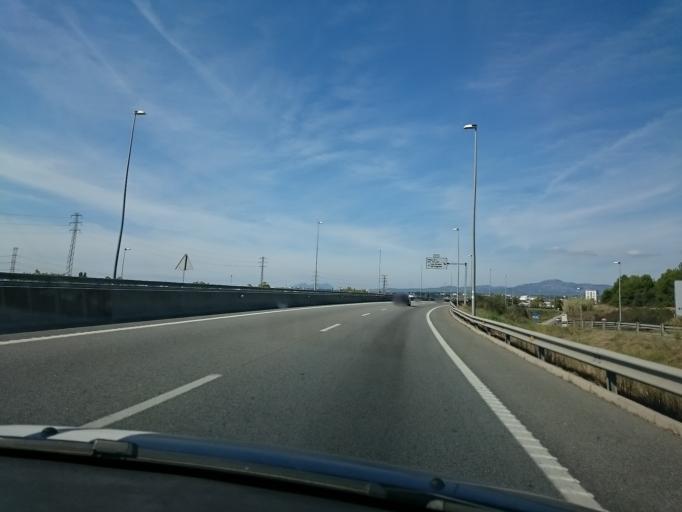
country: ES
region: Catalonia
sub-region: Provincia de Barcelona
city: Santa Perpetua de Mogoda
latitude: 41.5313
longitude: 2.1989
